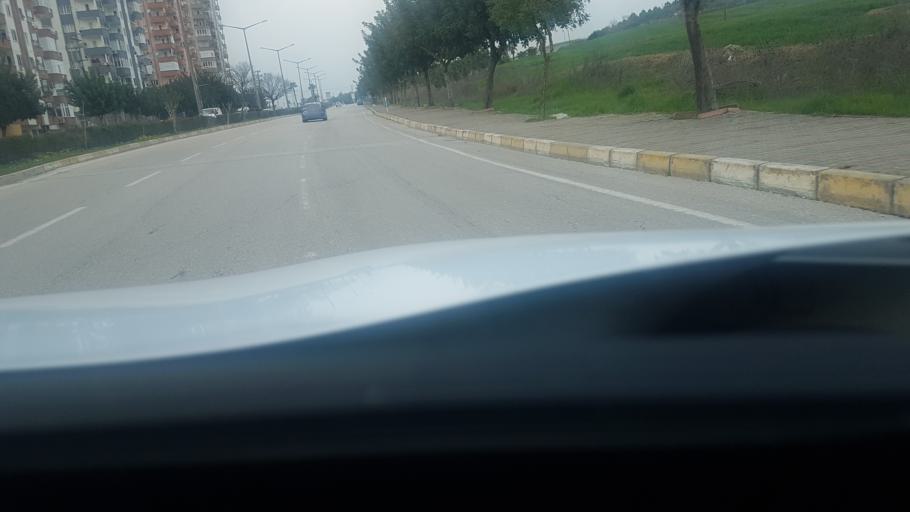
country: TR
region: Adana
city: Seyhan
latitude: 37.0538
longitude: 35.2507
